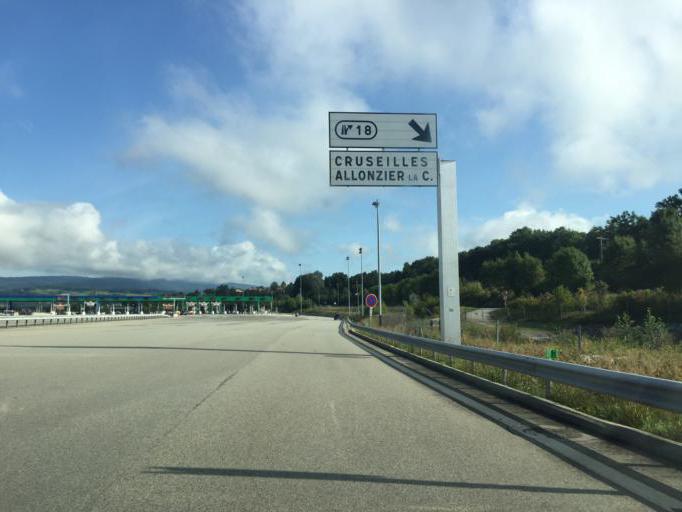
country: FR
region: Rhone-Alpes
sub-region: Departement de la Haute-Savoie
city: Allonzier-la-Caille
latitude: 45.9873
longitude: 6.1282
